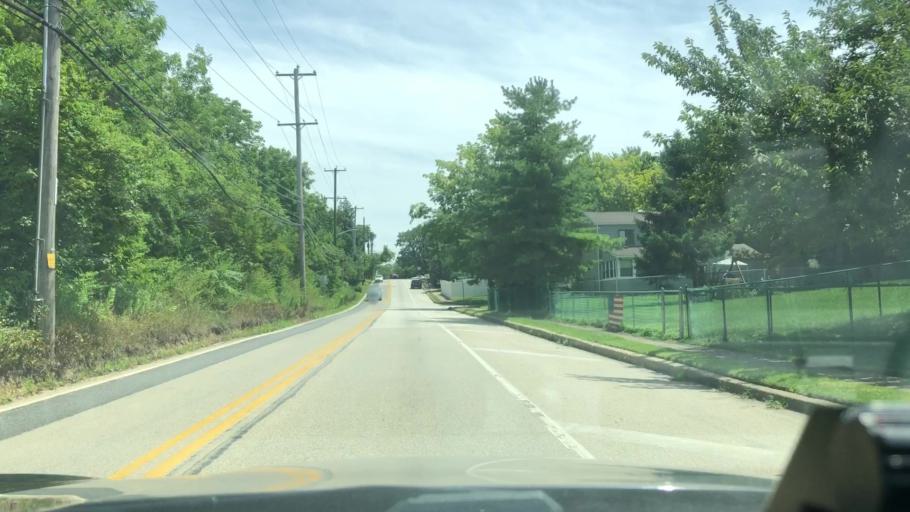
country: US
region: Pennsylvania
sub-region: Montgomery County
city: Plymouth Meeting
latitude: 40.1058
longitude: -75.2652
